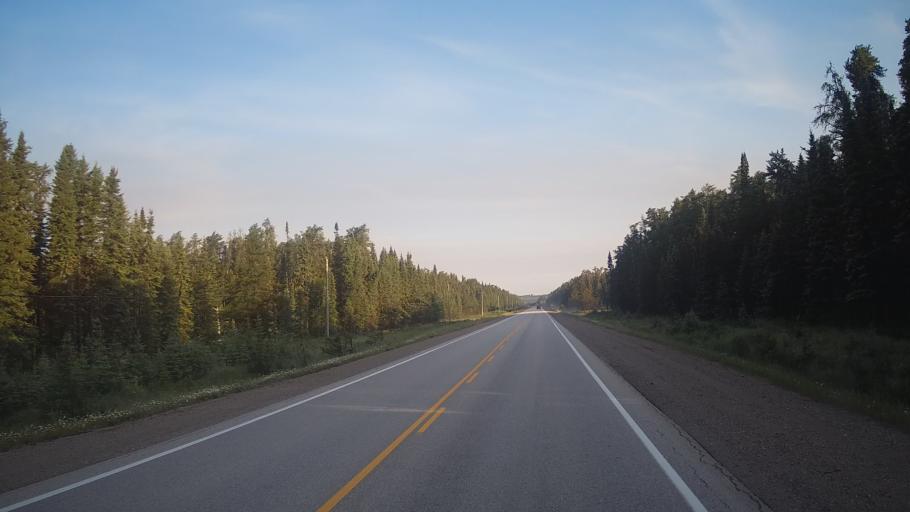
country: CA
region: Ontario
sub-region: Rainy River District
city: Atikokan
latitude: 49.2426
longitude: -91.0876
